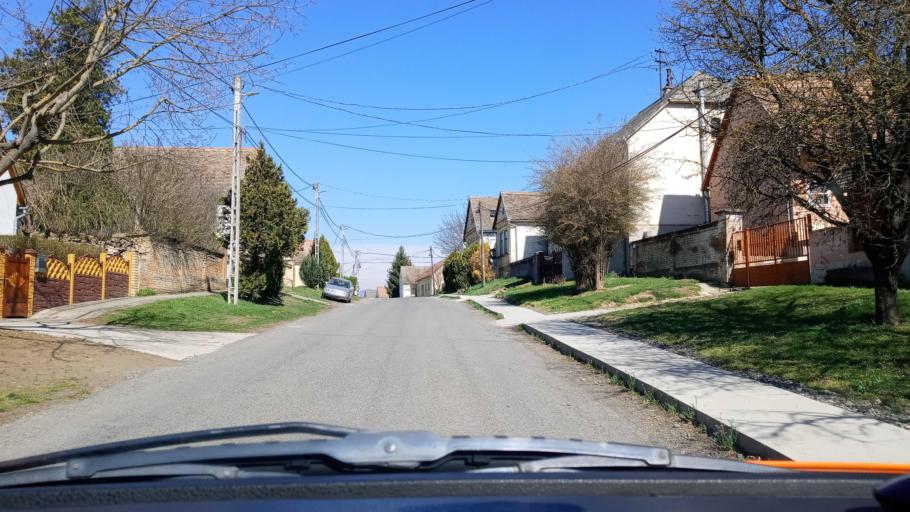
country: HU
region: Baranya
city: Boly
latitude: 46.0255
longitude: 18.4628
